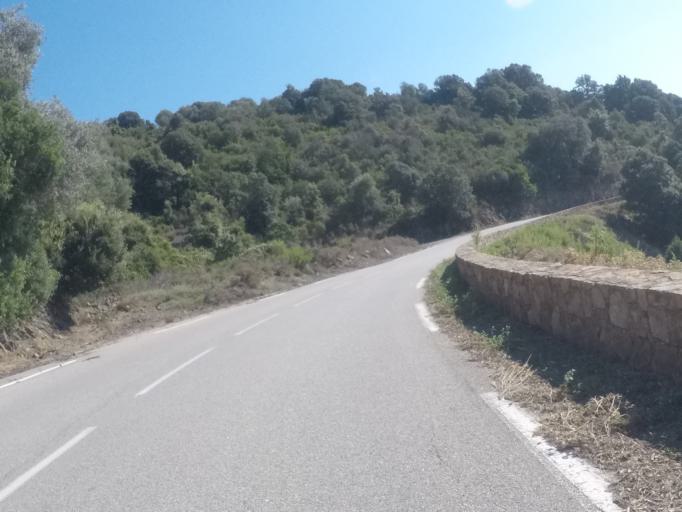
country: FR
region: Corsica
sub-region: Departement de la Corse-du-Sud
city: Cargese
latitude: 42.3190
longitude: 8.6624
